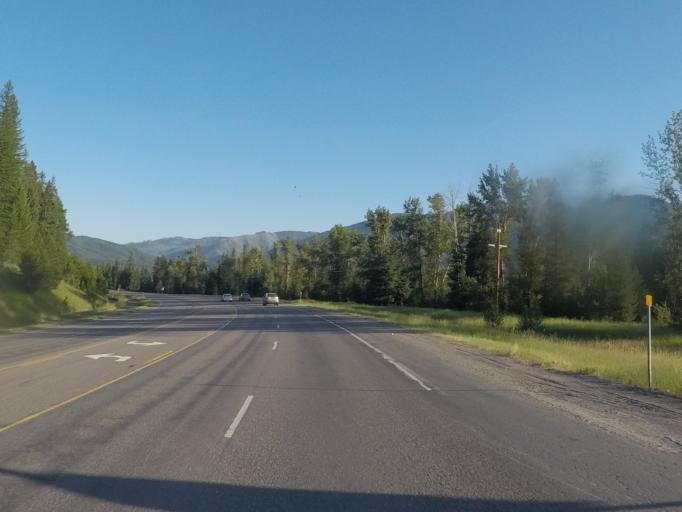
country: US
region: Montana
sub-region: Flathead County
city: Columbia Falls
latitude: 48.4136
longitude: -114.0494
